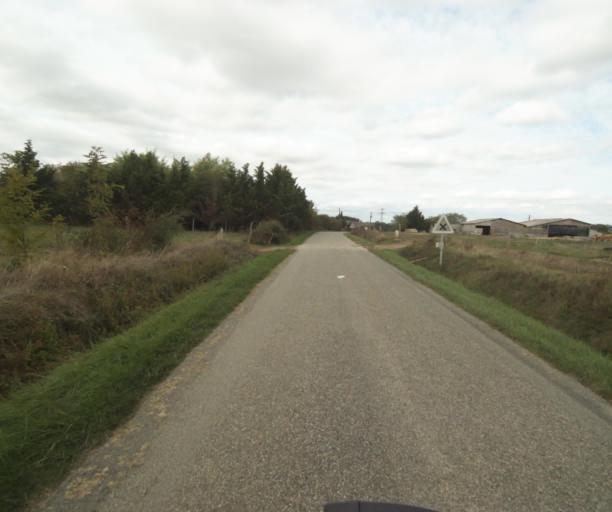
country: FR
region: Midi-Pyrenees
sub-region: Departement du Tarn-et-Garonne
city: Finhan
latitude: 43.8741
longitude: 1.1491
